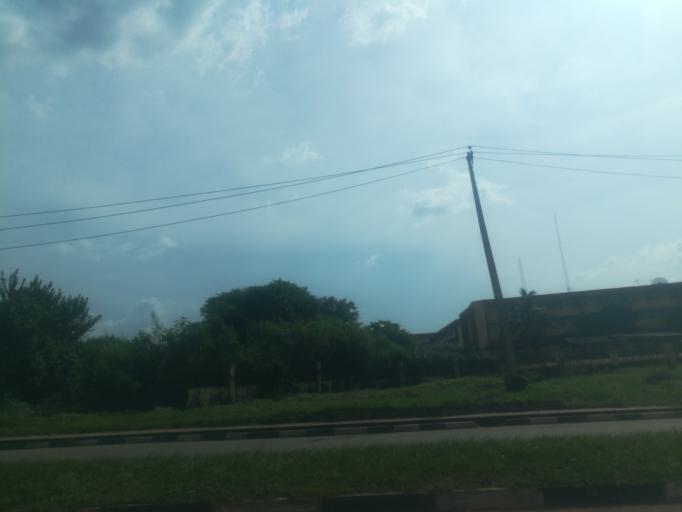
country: NG
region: Ogun
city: Abeokuta
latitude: 7.1226
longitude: 3.3672
